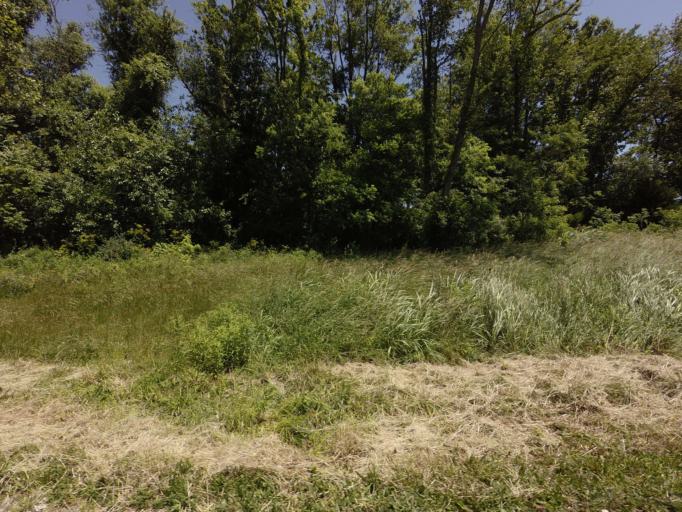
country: US
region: West Virginia
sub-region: Jefferson County
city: Ranson
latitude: 39.3181
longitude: -77.8234
